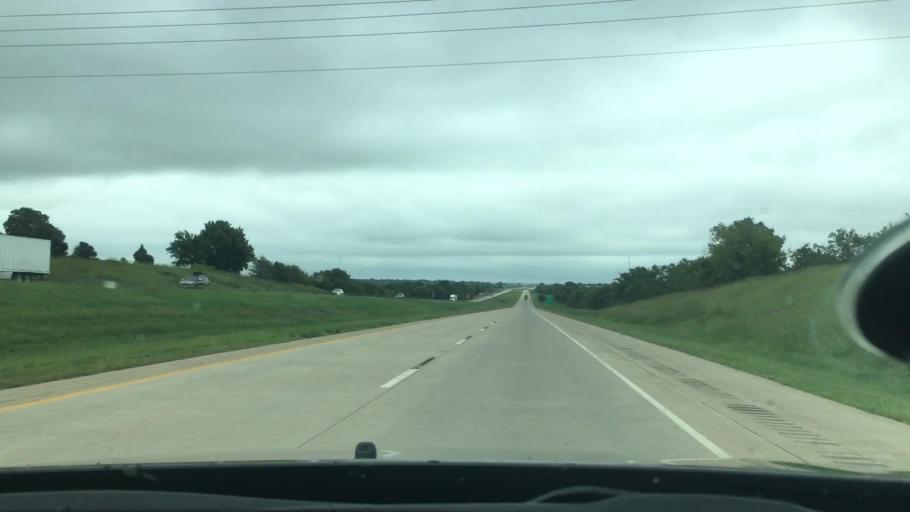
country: US
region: Oklahoma
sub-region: McIntosh County
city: Checotah
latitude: 35.4570
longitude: -95.5752
